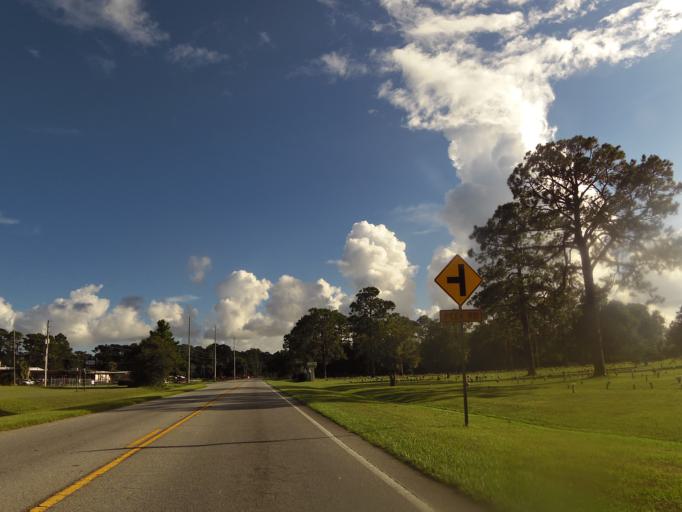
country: US
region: Georgia
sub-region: Glynn County
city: Country Club Estates
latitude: 31.2396
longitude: -81.4510
